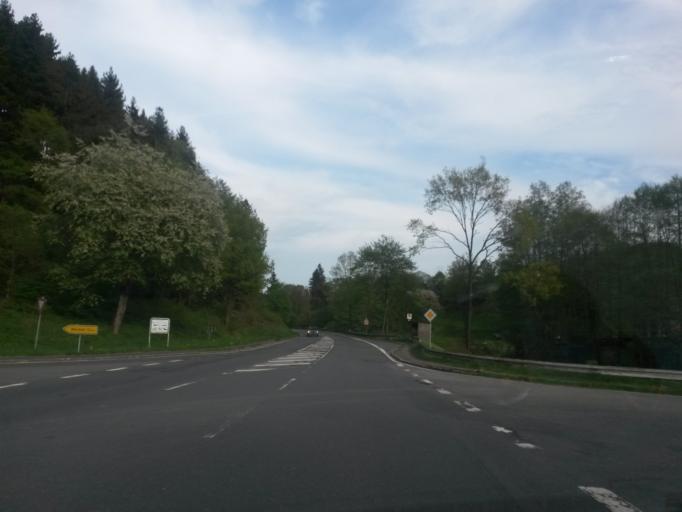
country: DE
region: North Rhine-Westphalia
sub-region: Regierungsbezirk Arnsberg
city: Herscheid
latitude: 51.1856
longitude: 7.7173
